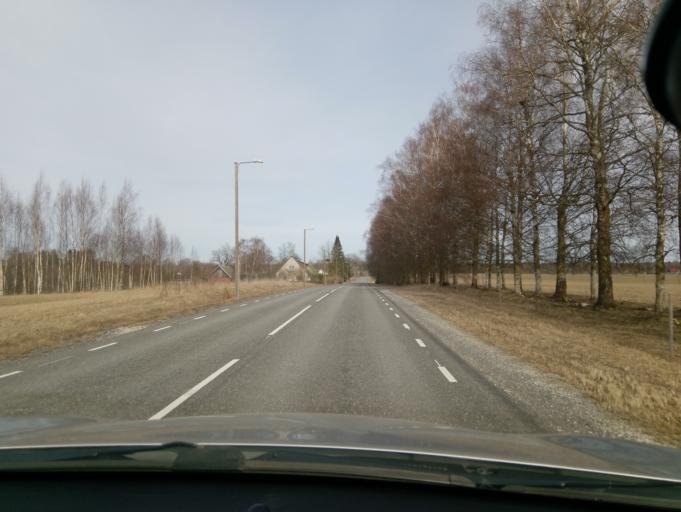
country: EE
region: Jaervamaa
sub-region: Tueri vald
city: Tueri
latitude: 58.8452
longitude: 25.3559
